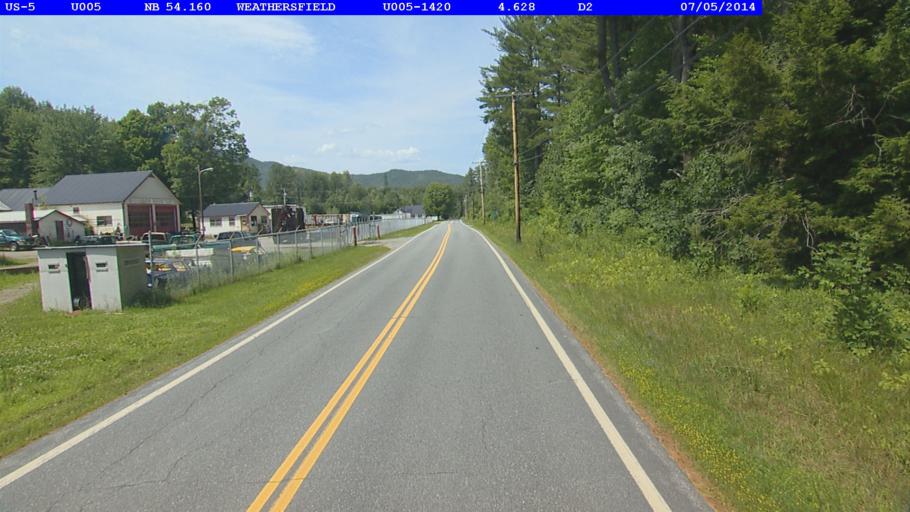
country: US
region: New Hampshire
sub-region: Sullivan County
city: Claremont
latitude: 43.3990
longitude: -72.4052
